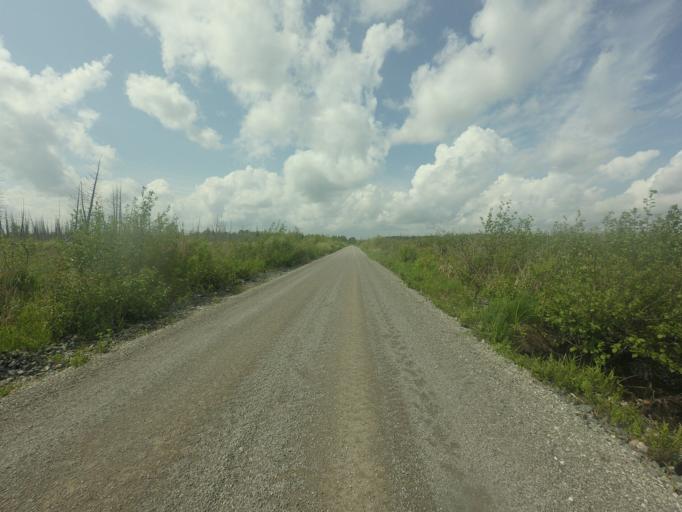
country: CA
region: Ontario
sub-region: Lanark County
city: Smiths Falls
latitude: 45.0093
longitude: -76.0702
